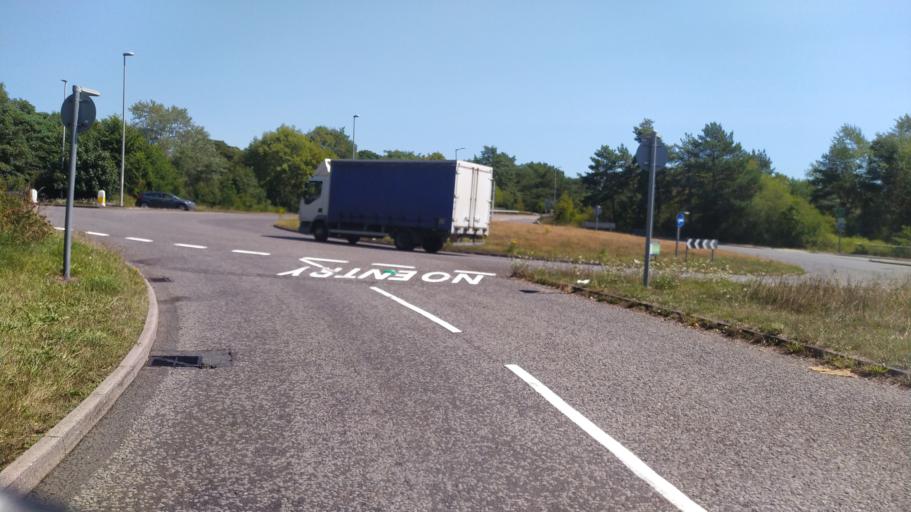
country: GB
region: England
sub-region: Dorset
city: Broadstone
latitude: 50.7403
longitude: -2.0143
